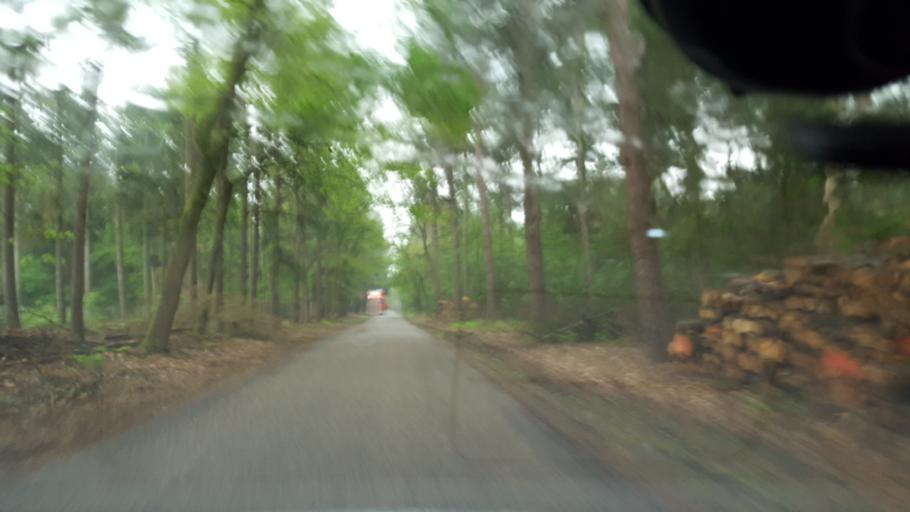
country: NL
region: North Brabant
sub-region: Gemeente Someren
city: Someren
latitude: 51.3992
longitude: 5.6691
